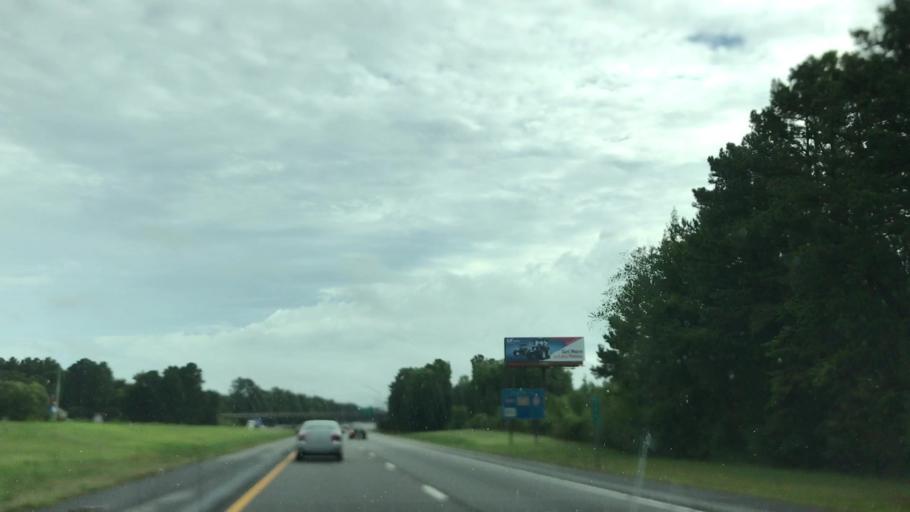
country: US
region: North Carolina
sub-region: Nash County
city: Red Oak
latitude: 36.0577
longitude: -77.8267
